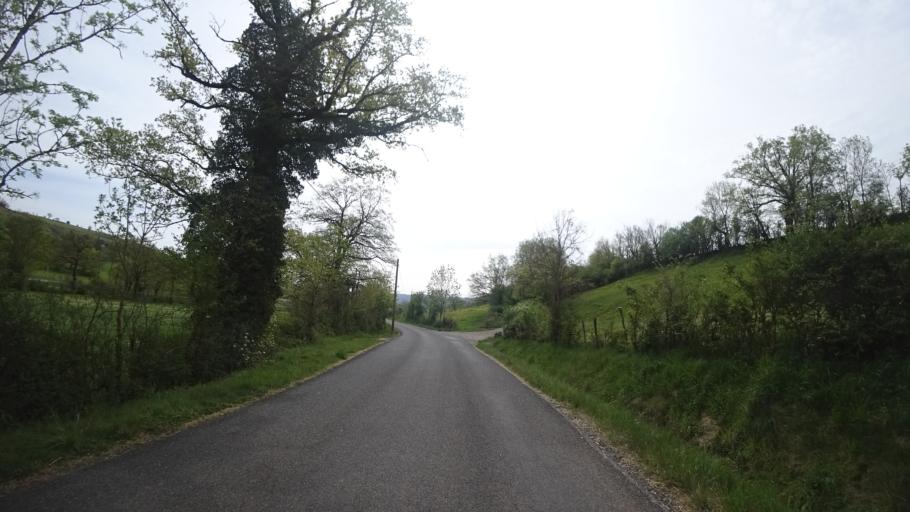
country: FR
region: Midi-Pyrenees
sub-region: Departement de l'Aveyron
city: Sainte-Radegonde
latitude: 44.3718
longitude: 2.6235
